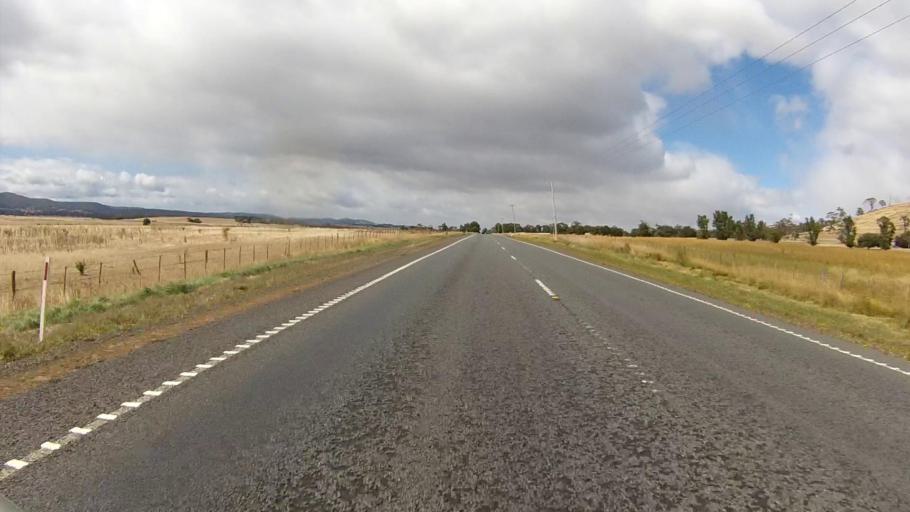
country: AU
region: Tasmania
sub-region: Northern Midlands
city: Evandale
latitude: -41.9755
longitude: 147.5034
